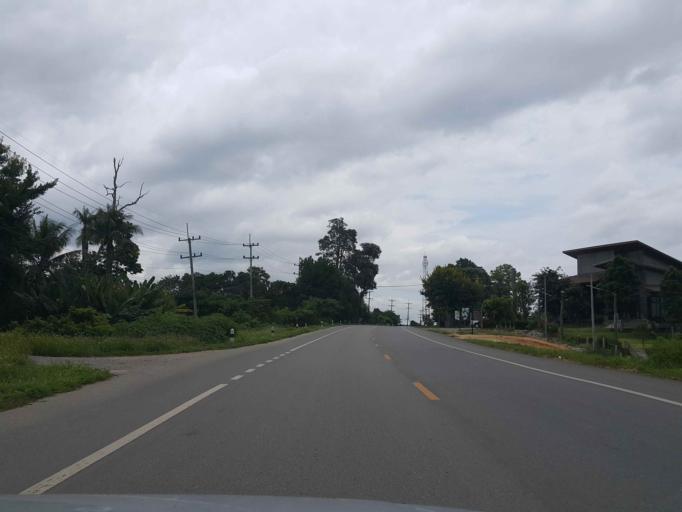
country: TH
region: Lamphun
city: Li
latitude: 17.7882
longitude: 98.9532
